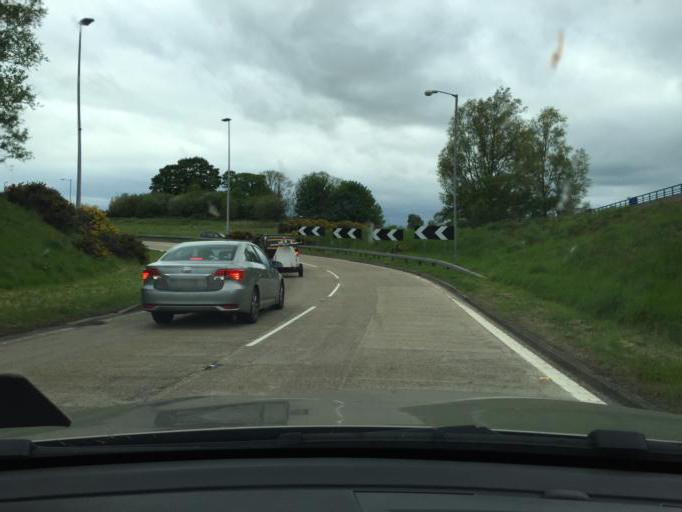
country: GB
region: Northern Ireland
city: Hillsborough
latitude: 54.4936
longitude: -6.0612
